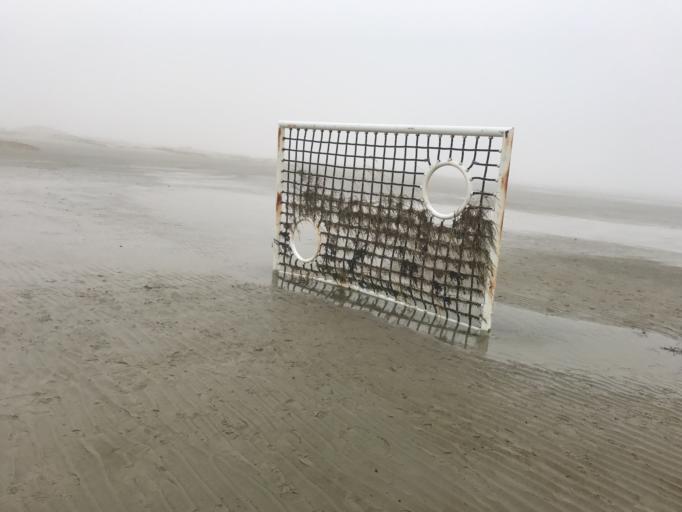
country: DE
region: Lower Saxony
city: Borkum
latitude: 53.6023
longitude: 6.6715
